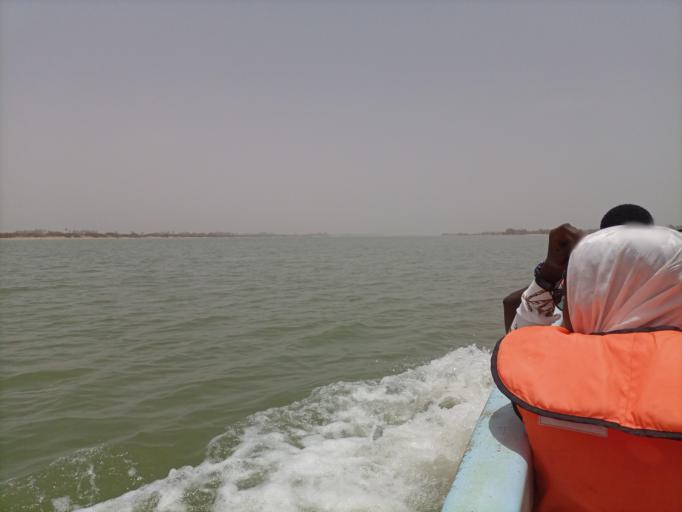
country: SN
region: Saint-Louis
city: Saint-Louis
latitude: 15.8611
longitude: -16.5160
